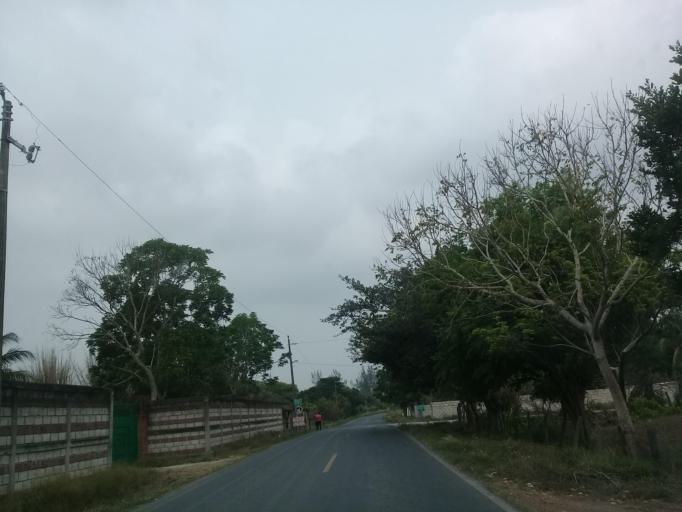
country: MX
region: Veracruz
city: El Tejar
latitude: 19.0545
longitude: -96.1976
